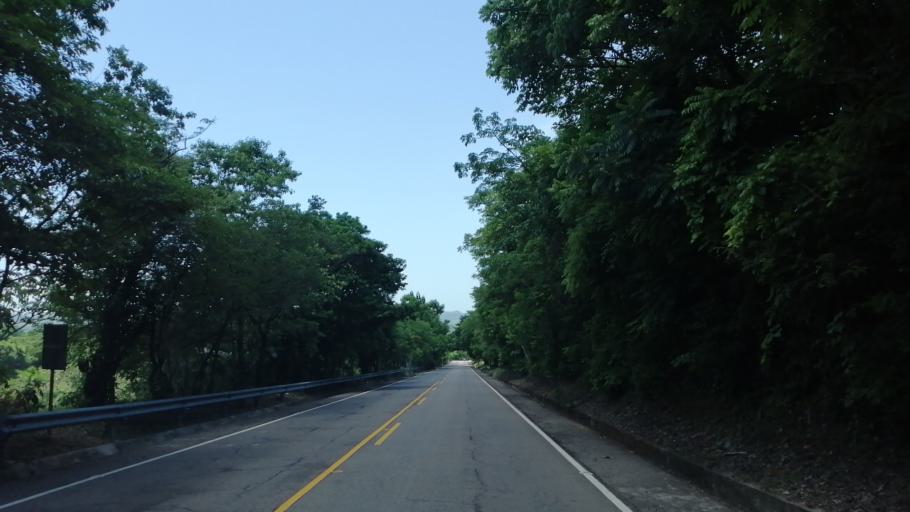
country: SV
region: Chalatenango
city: Nueva Concepcion
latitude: 14.1578
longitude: -89.3094
